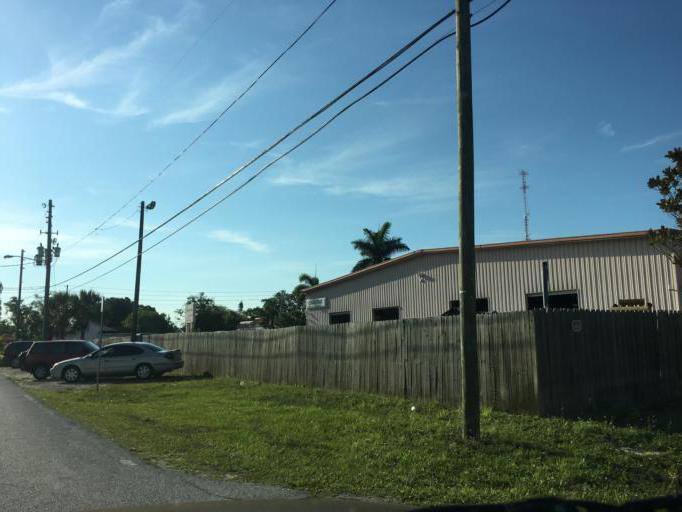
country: US
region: Florida
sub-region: Pinellas County
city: Pinellas Park
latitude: 27.8338
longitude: -82.7010
